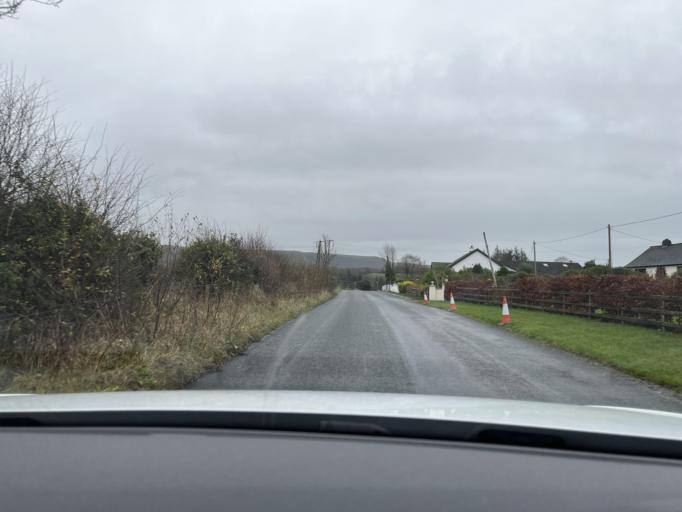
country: IE
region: Connaught
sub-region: County Leitrim
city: Manorhamilton
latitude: 54.2973
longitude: -8.1994
